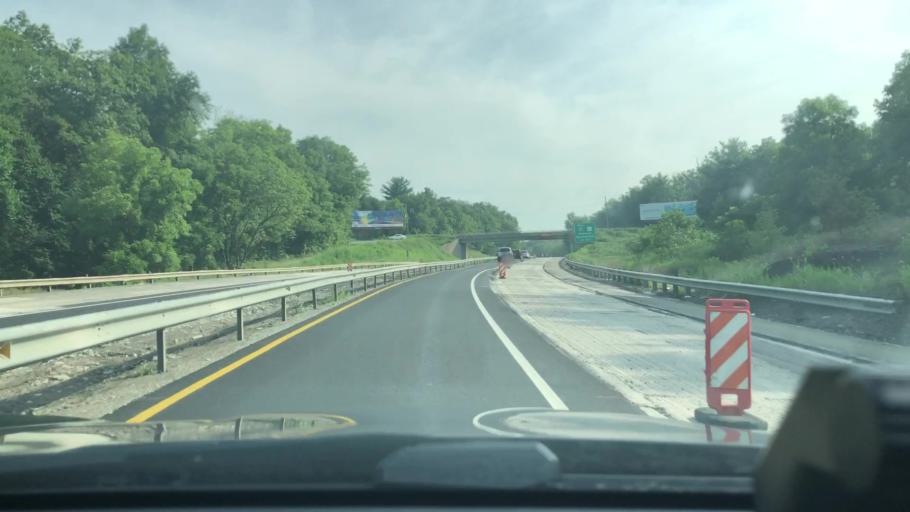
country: US
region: Pennsylvania
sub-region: Monroe County
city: Arlington Heights
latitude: 40.9788
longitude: -75.2750
